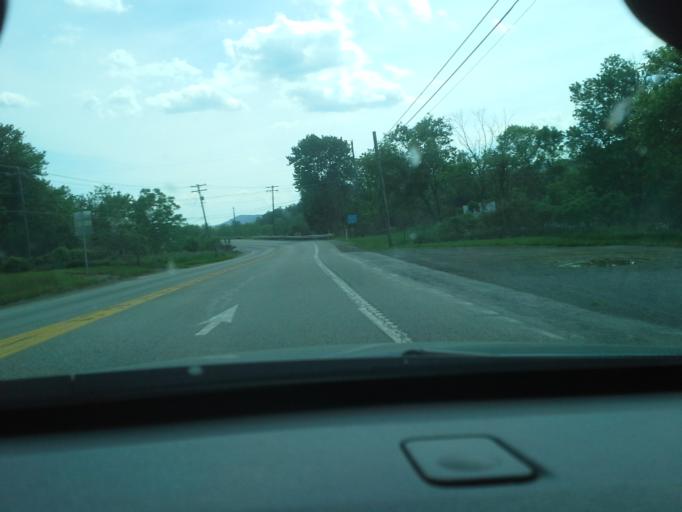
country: US
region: Pennsylvania
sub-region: Fulton County
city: McConnellsburg
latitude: 39.9418
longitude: -77.9955
